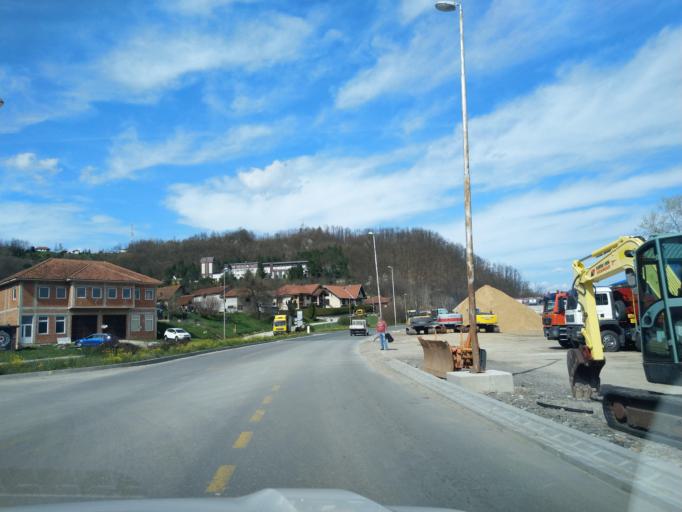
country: RS
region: Central Serbia
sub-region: Zlatiborski Okrug
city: Arilje
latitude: 43.7647
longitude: 20.0949
